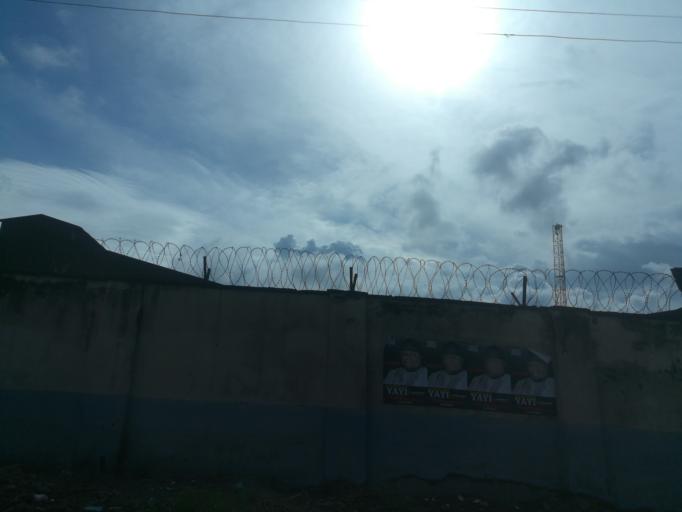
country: NG
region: Lagos
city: Agege
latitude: 6.6261
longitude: 3.3496
